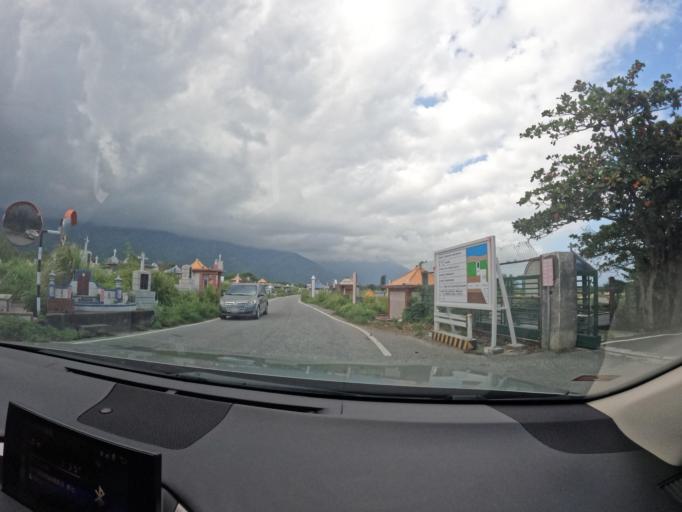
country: TW
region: Taiwan
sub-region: Hualien
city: Hualian
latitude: 24.0516
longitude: 121.6160
